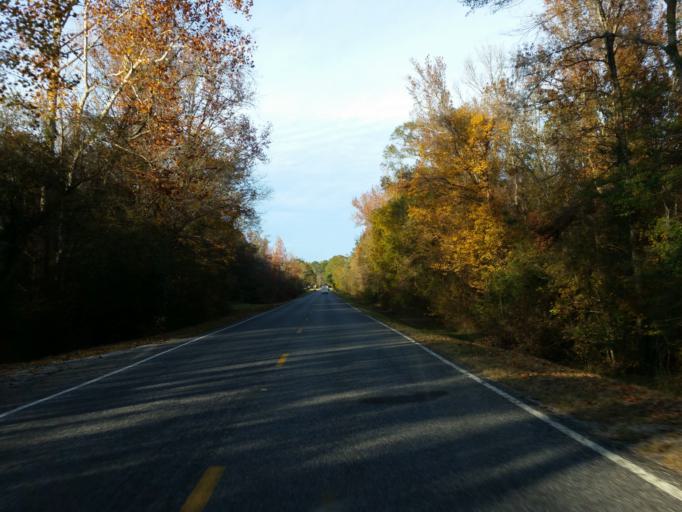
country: US
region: Mississippi
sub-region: Clarke County
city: Stonewall
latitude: 32.0643
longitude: -88.8800
